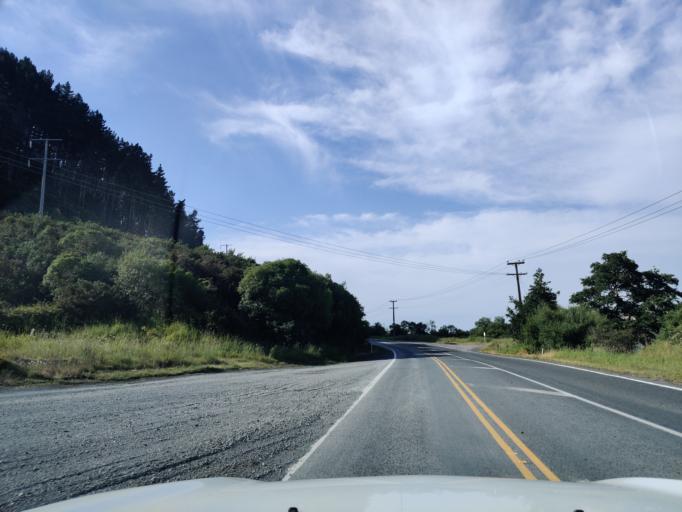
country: NZ
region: Waikato
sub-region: Waikato District
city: Ngaruawahia
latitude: -37.5910
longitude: 175.1552
